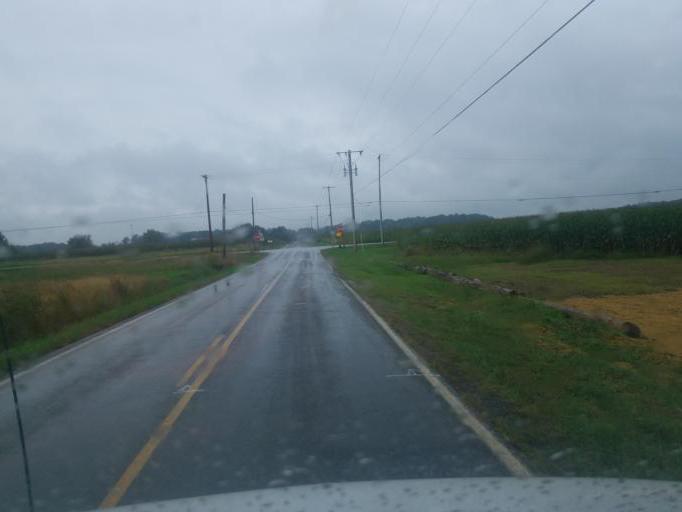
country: US
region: Ohio
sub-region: Wayne County
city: Rittman
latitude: 41.0092
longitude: -81.8151
